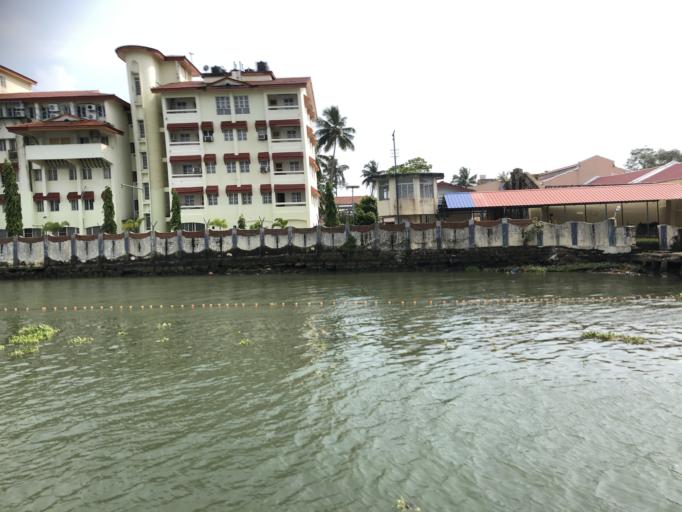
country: IN
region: Kerala
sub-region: Ernakulam
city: Cochin
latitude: 9.9695
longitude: 76.2474
